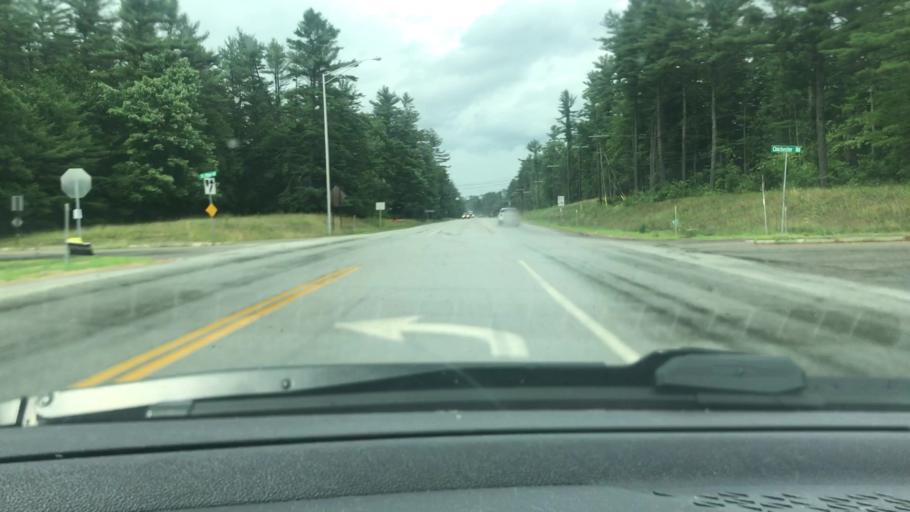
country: US
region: New Hampshire
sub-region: Merrimack County
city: Chichester
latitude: 43.2751
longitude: -71.4617
